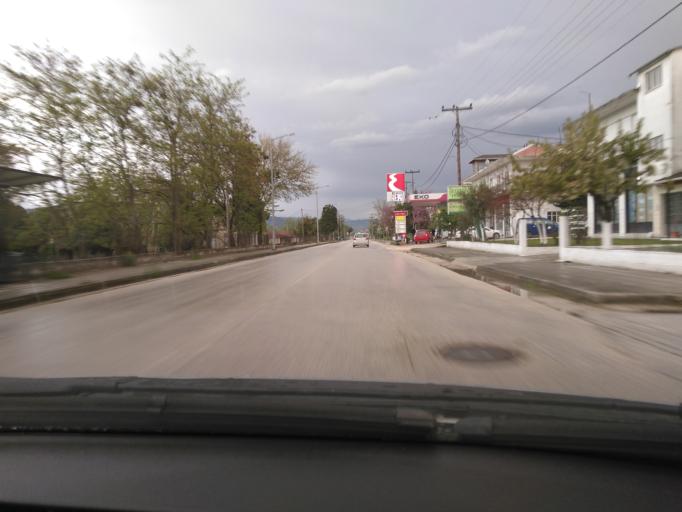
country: GR
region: Epirus
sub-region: Nomos Ioanninon
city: Anatoli
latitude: 39.6322
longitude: 20.8762
